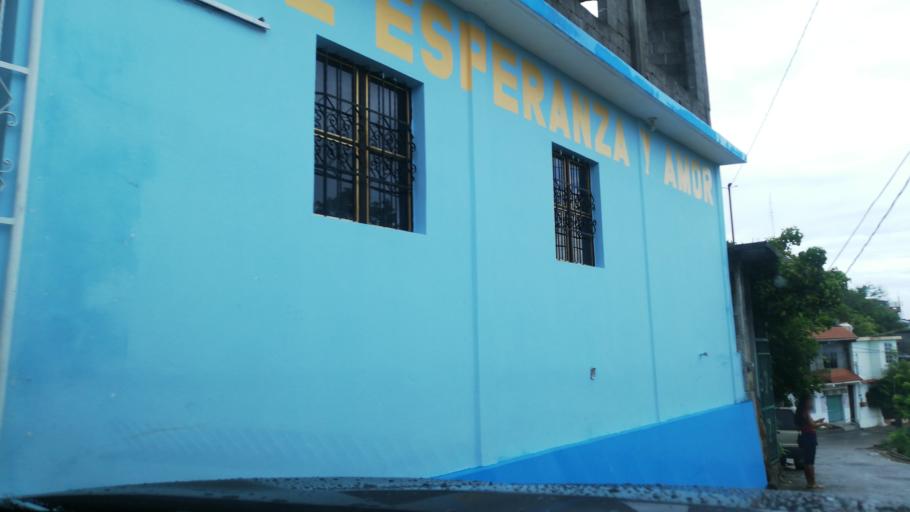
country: MX
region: Oaxaca
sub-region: Salina Cruz
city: Salina Cruz
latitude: 16.1867
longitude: -95.1933
